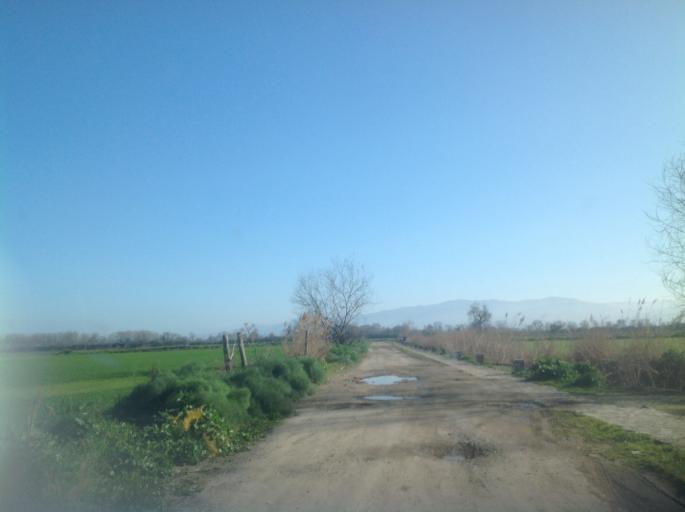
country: IT
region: Calabria
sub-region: Provincia di Cosenza
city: Sibari
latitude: 39.7205
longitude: 16.4960
